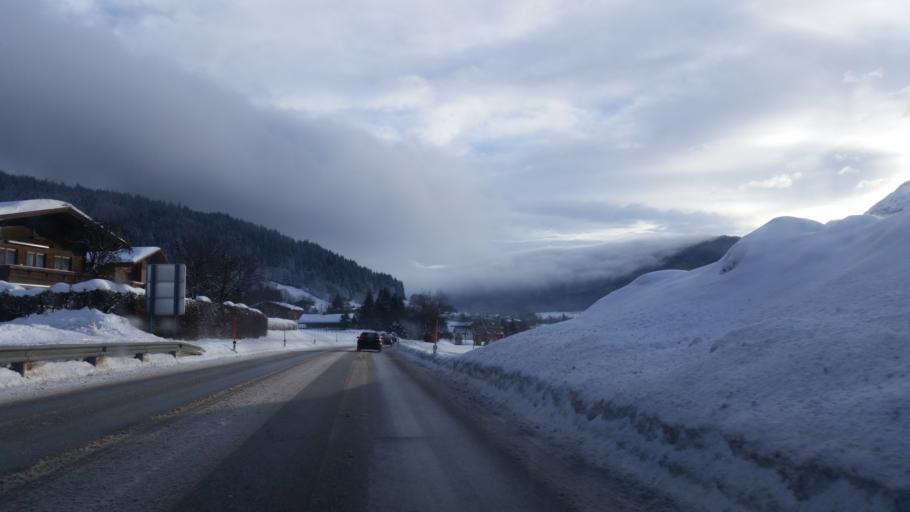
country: AT
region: Tyrol
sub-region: Politischer Bezirk Kitzbuhel
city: Hochfilzen
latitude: 47.4681
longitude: 12.5821
